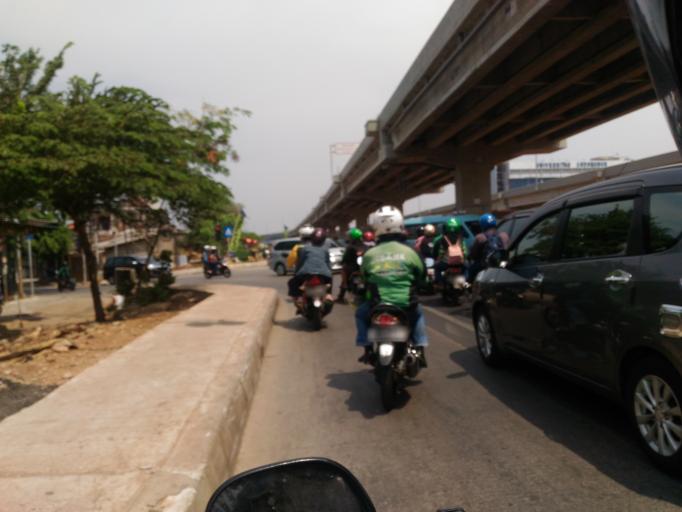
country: ID
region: Jakarta Raya
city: Jakarta
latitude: -6.2416
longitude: 106.8964
